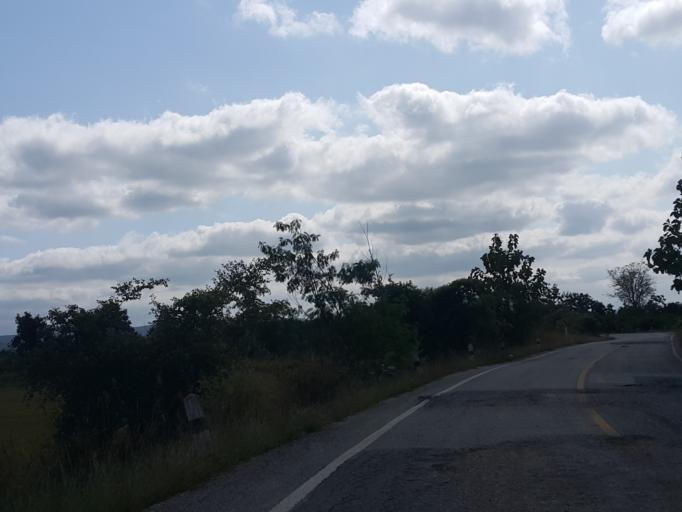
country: TH
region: Lamphun
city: Lamphun
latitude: 18.5424
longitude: 99.0877
